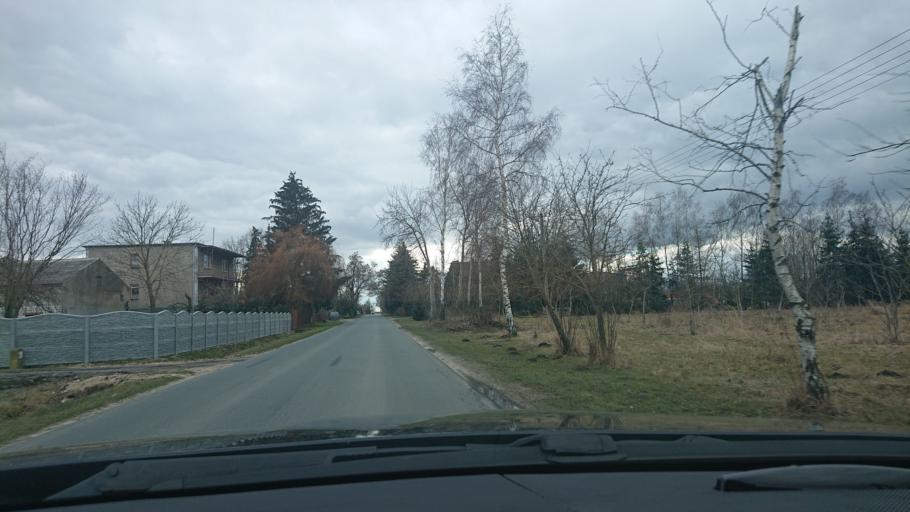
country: PL
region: Greater Poland Voivodeship
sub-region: Powiat gnieznienski
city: Gniezno
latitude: 52.5756
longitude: 17.6251
